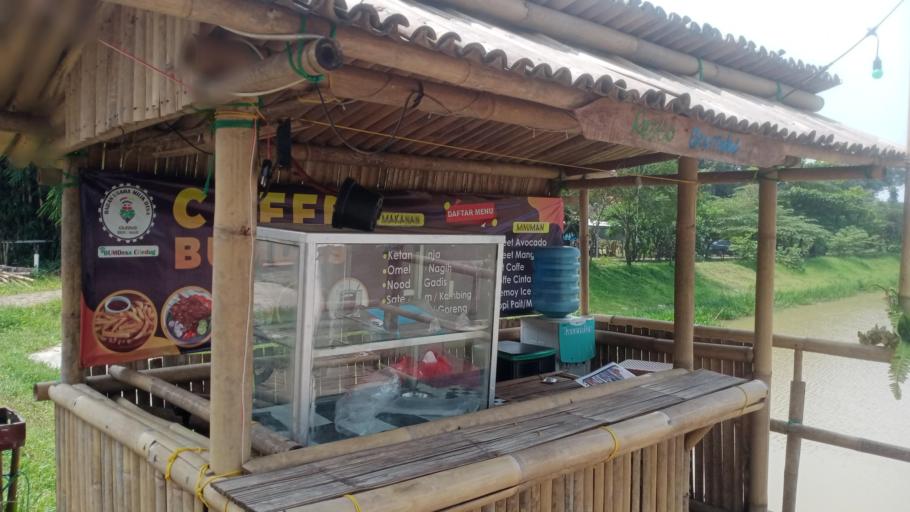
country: ID
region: West Java
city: Cileungsir
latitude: -6.3502
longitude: 107.0362
